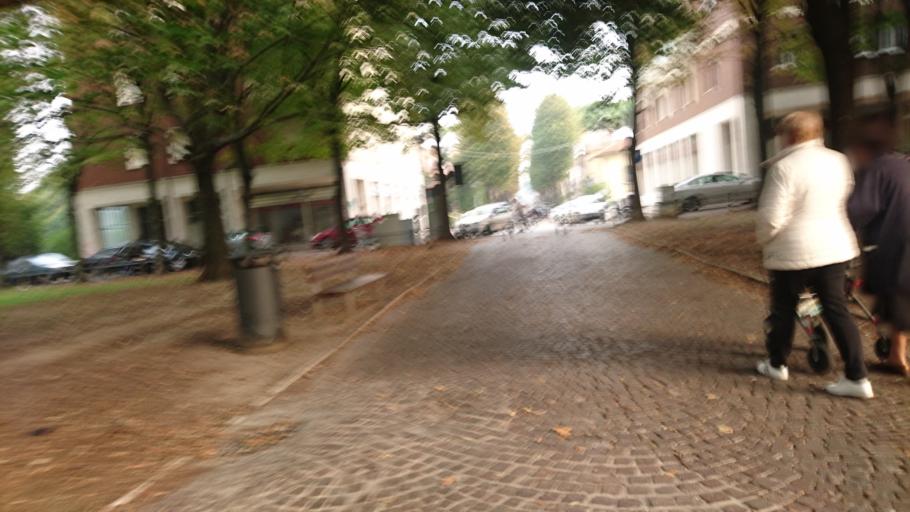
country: IT
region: Emilia-Romagna
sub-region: Provincia di Rimini
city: Rimini
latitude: 44.0578
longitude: 12.5741
